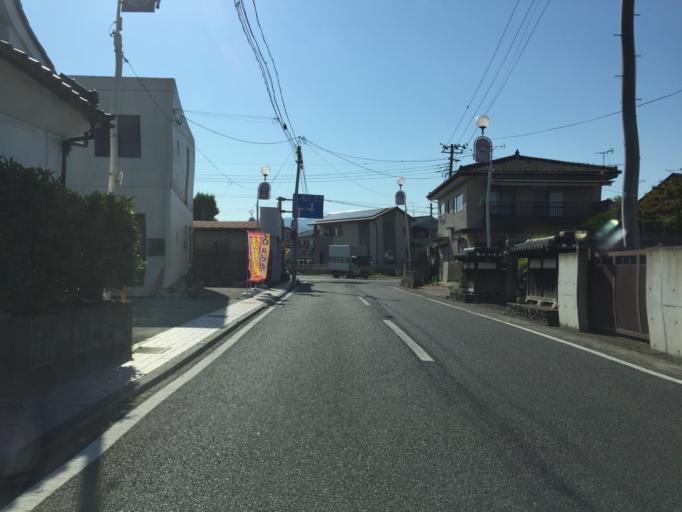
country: JP
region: Ibaraki
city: Kitaibaraki
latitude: 36.8915
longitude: 140.7613
